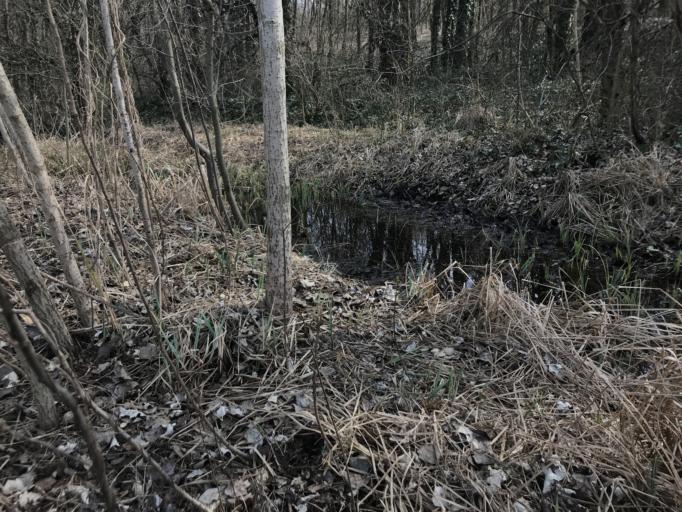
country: HU
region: Budapest
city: Budapest XV. keruelet
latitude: 47.5894
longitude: 19.1072
